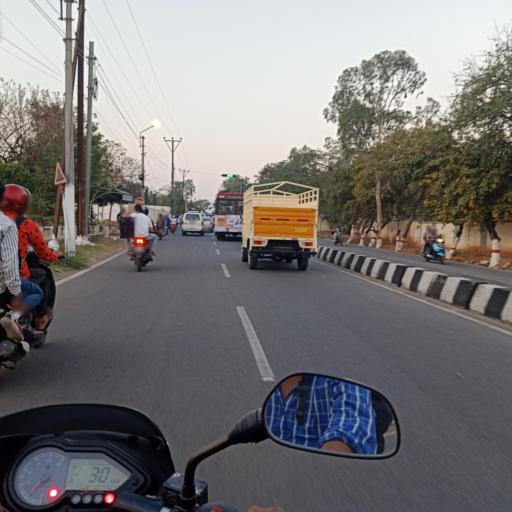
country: IN
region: Telangana
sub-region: Rangareddi
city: Secunderabad
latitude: 17.4839
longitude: 78.5113
